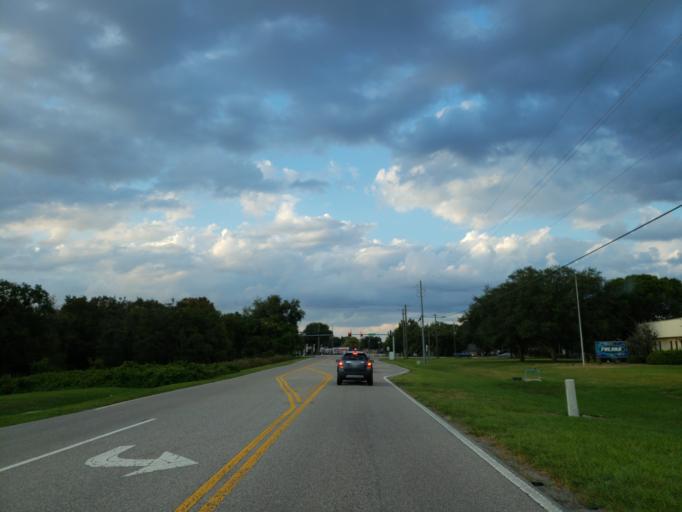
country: US
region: Florida
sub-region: Pasco County
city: Odessa
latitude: 28.1862
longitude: -82.5919
